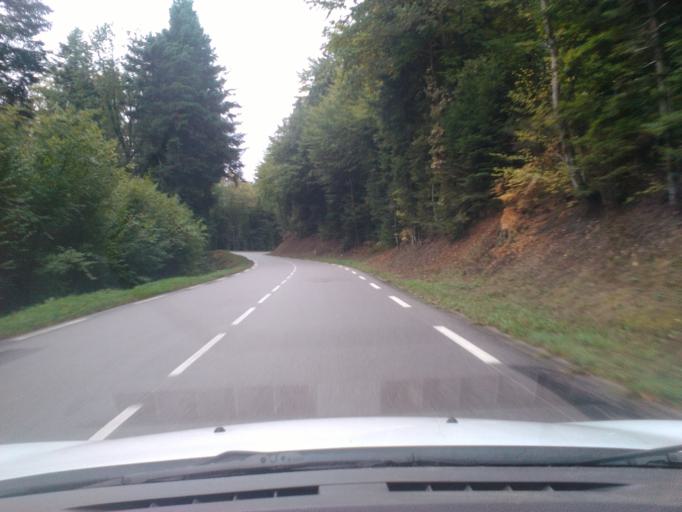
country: FR
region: Lorraine
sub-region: Departement des Vosges
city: Taintrux
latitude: 48.2732
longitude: 6.8880
